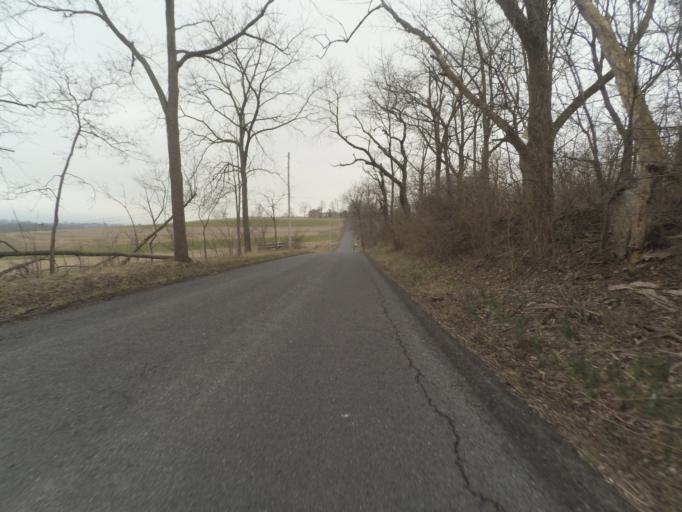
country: US
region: Pennsylvania
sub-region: Centre County
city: Boalsburg
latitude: 40.7986
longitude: -77.7693
